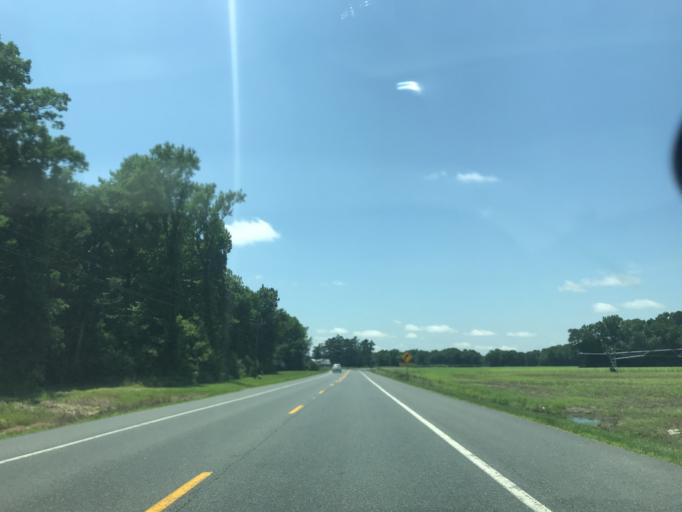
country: US
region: Maryland
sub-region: Caroline County
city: Federalsburg
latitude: 38.6327
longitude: -75.7159
